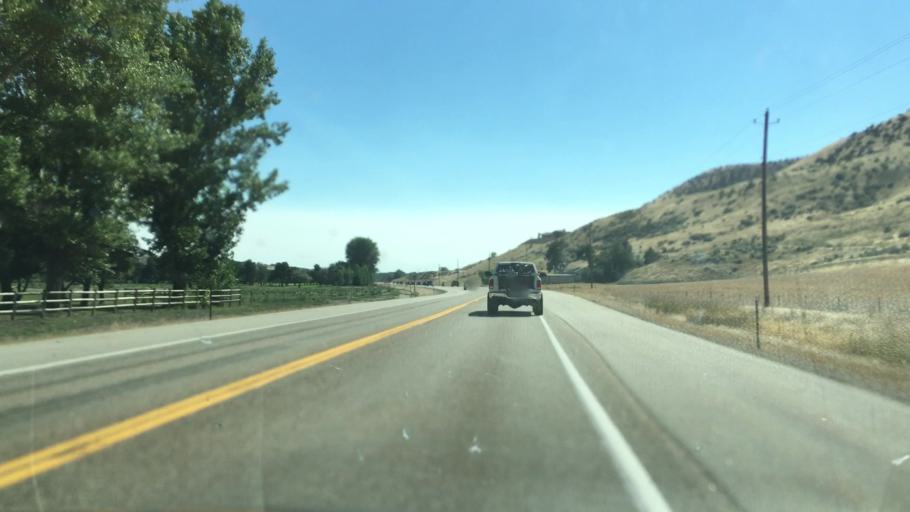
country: US
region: Idaho
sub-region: Ada County
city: Eagle
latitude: 43.7453
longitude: -116.2974
